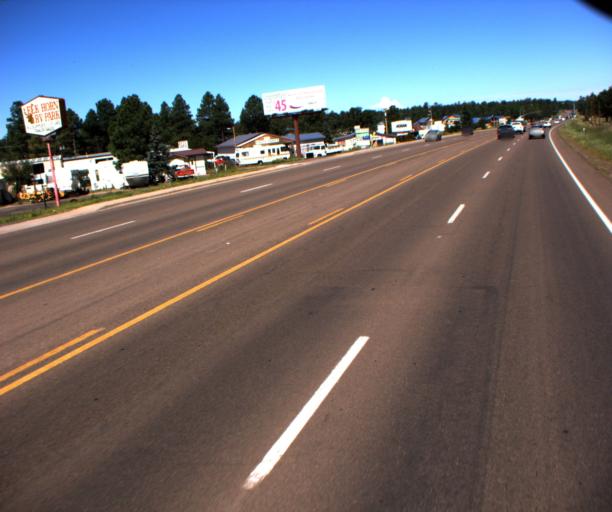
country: US
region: Arizona
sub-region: Navajo County
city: Lake of the Woods
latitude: 34.1704
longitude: -110.0011
